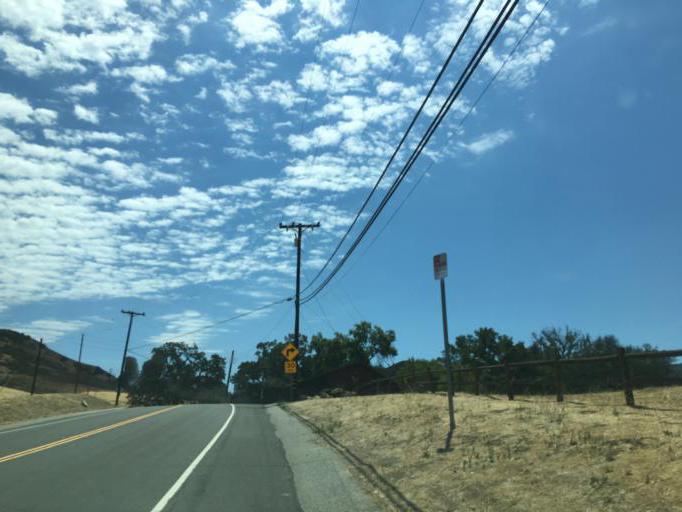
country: US
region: California
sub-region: Los Angeles County
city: Agoura Hills
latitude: 34.1151
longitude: -118.7527
